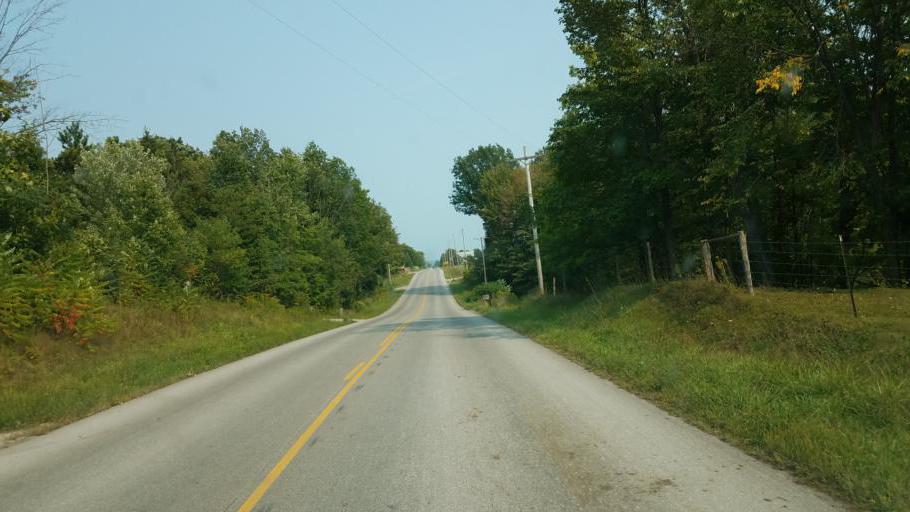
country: US
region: Ohio
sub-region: Geauga County
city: Middlefield
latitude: 41.5087
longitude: -80.9977
